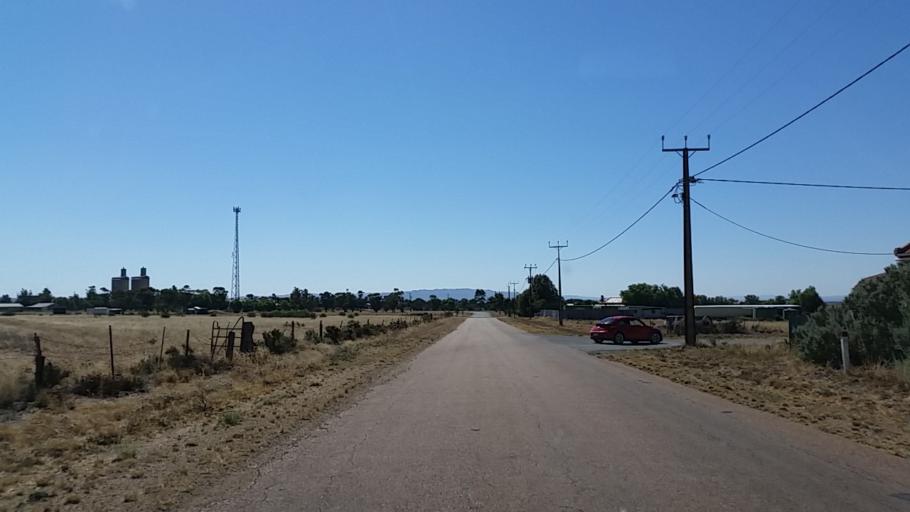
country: AU
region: South Australia
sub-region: Peterborough
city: Peterborough
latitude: -32.7369
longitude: 138.6217
